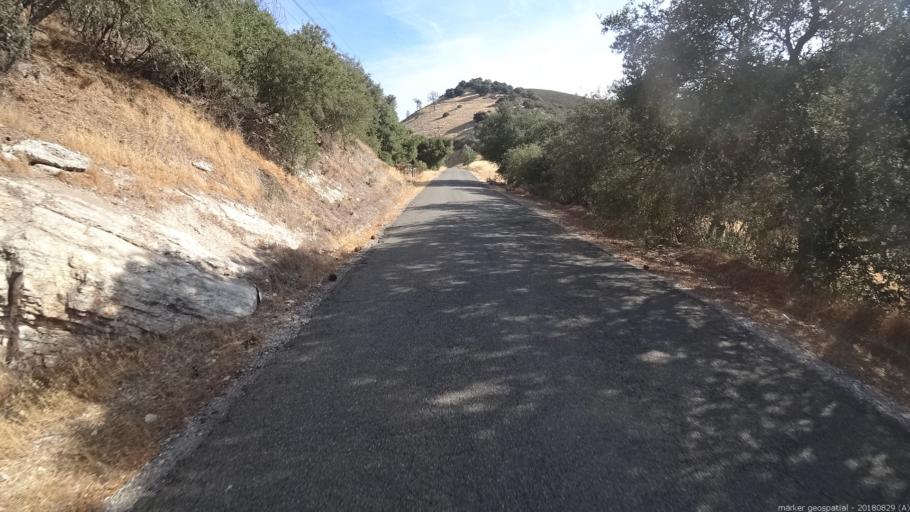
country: US
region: California
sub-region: Monterey County
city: King City
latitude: 36.0002
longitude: -121.0680
